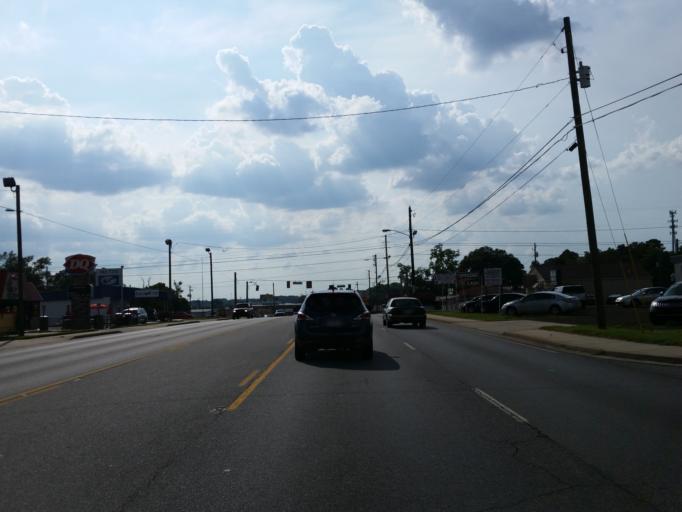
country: US
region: Georgia
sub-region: Tift County
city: Tifton
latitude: 31.4502
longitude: -83.5151
